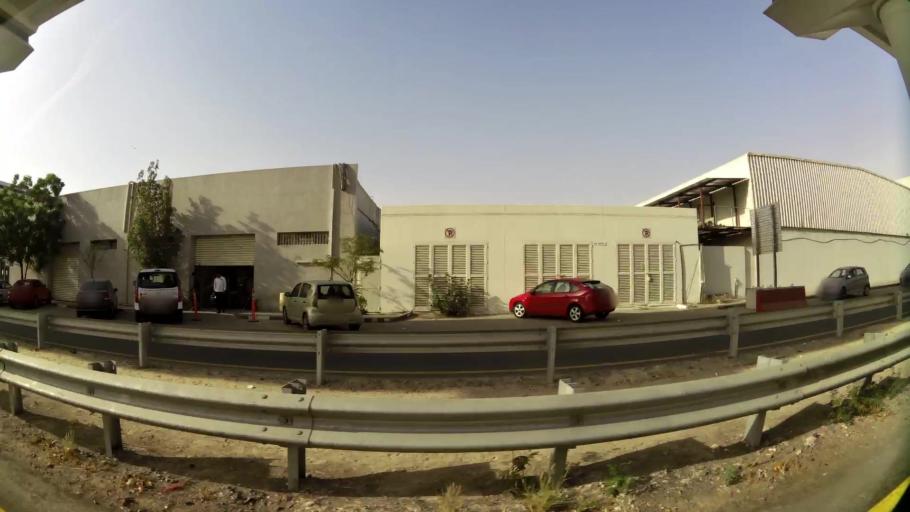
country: AE
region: Ash Shariqah
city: Sharjah
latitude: 25.2394
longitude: 55.3687
